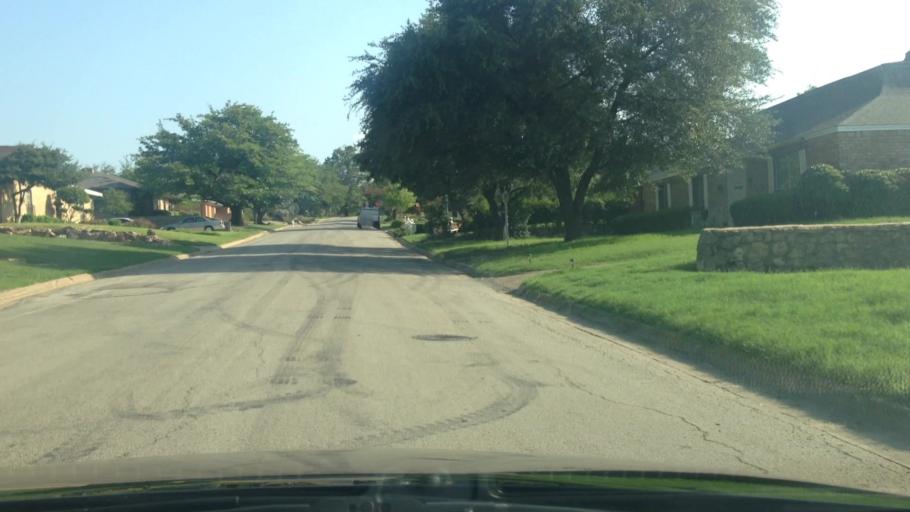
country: US
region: Texas
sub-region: Tarrant County
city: Edgecliff Village
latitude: 32.6588
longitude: -97.3387
